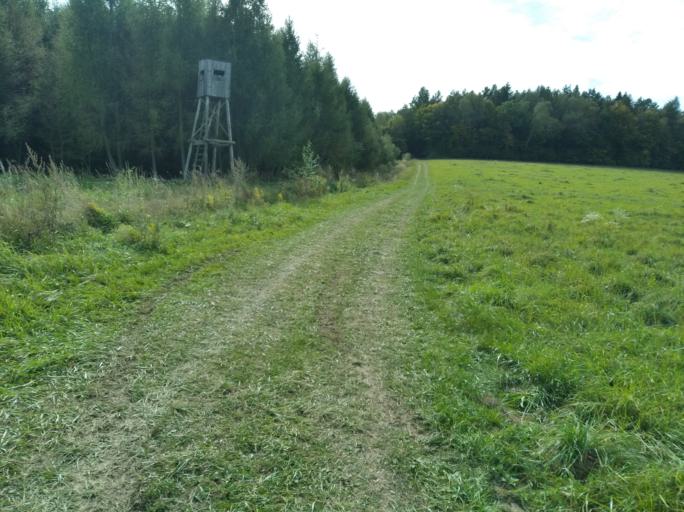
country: PL
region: Subcarpathian Voivodeship
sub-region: Powiat strzyzowski
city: Jawornik
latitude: 49.8295
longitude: 21.9063
